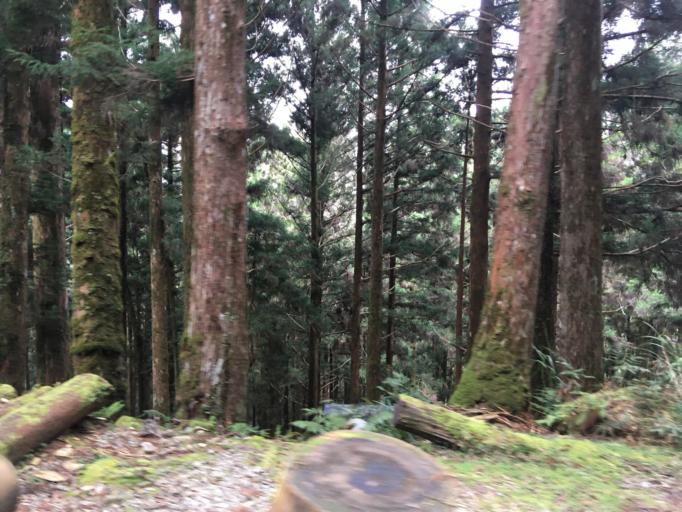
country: TW
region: Taiwan
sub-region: Yilan
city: Yilan
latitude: 24.4790
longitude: 121.5366
